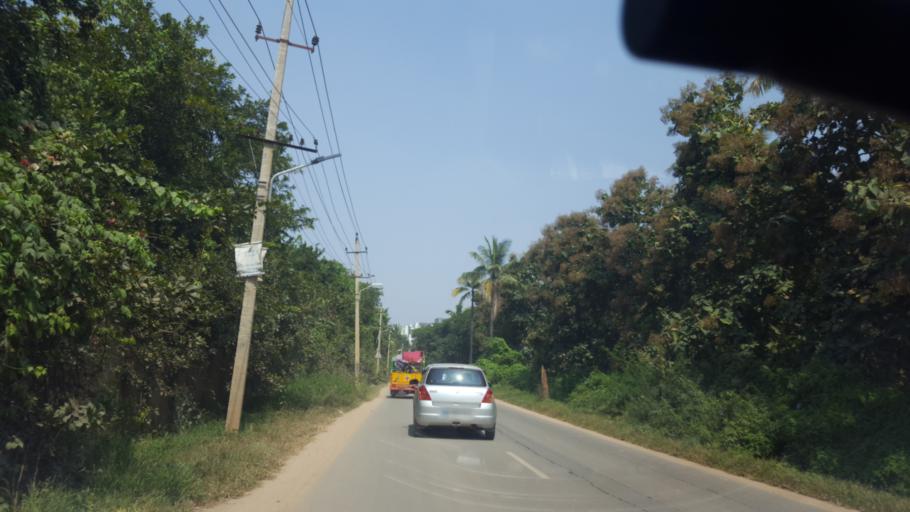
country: IN
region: Karnataka
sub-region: Bangalore Urban
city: Bangalore
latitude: 12.9367
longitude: 77.7105
